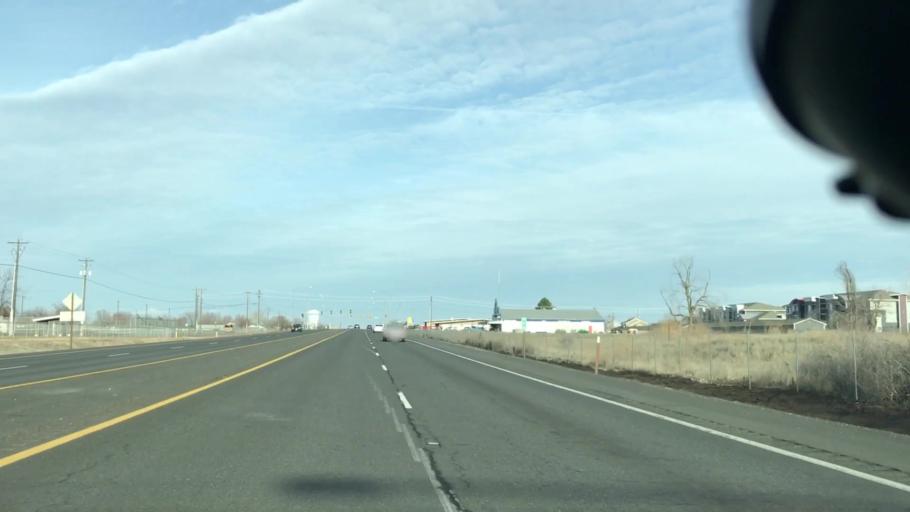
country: US
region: Washington
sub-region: Grant County
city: Moses Lake
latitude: 47.1132
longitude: -119.2567
